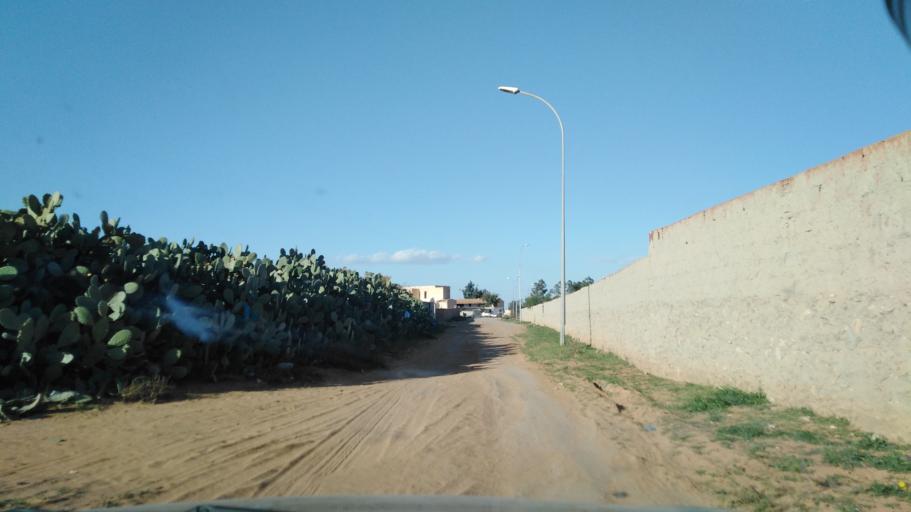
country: TN
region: Al Mahdiyah
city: Shurban
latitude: 34.9584
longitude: 10.3630
